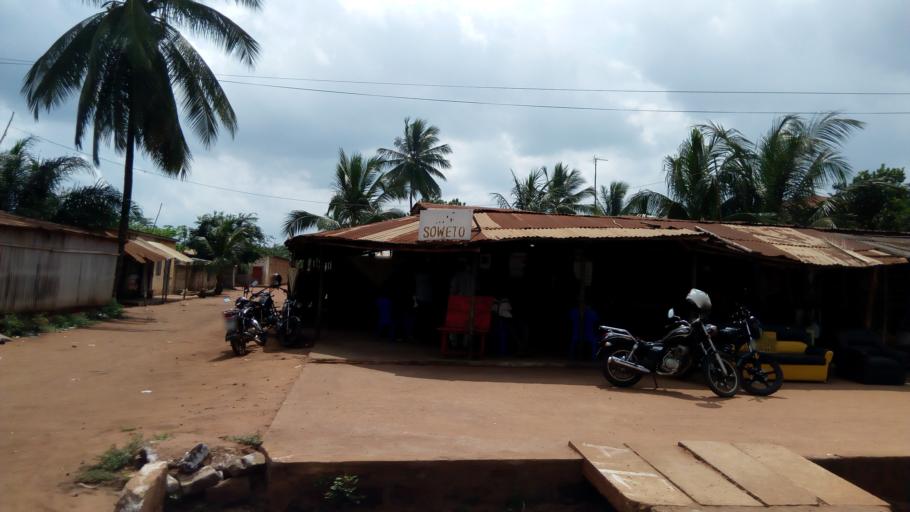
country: TG
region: Maritime
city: Tsevie
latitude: 6.4331
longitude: 1.2122
